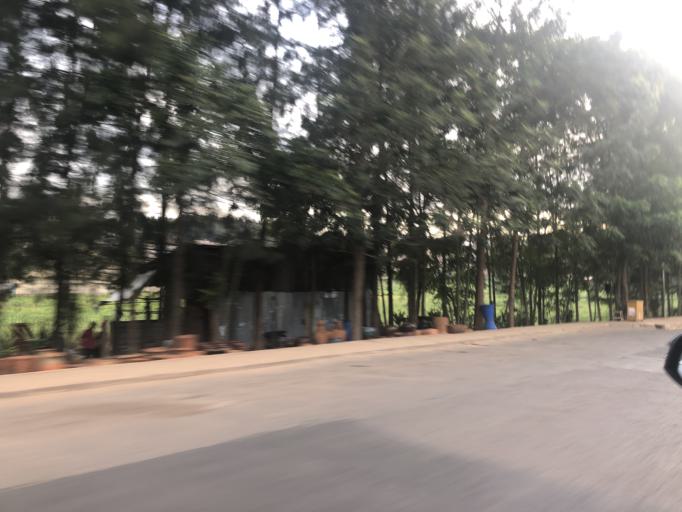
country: RW
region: Kigali
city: Kigali
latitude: -1.9317
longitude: 30.0857
